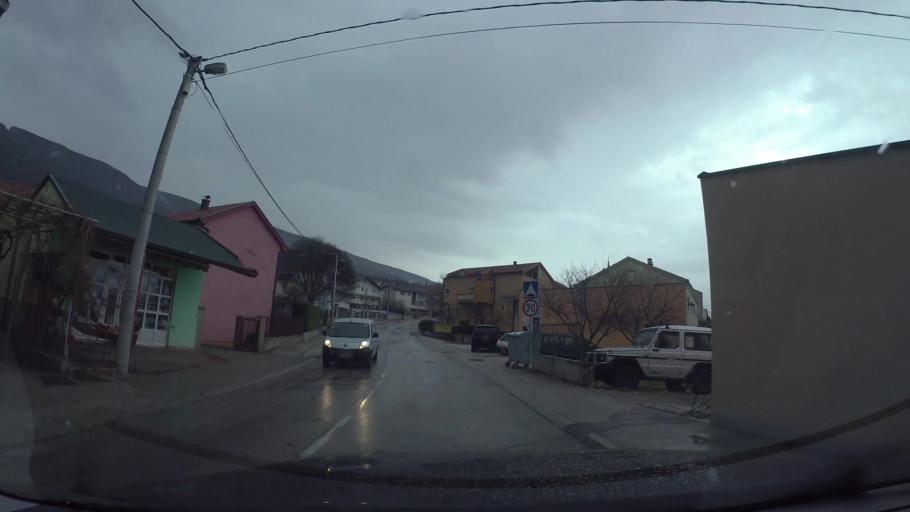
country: BA
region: Federation of Bosnia and Herzegovina
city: Rodoc
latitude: 43.3186
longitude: 17.8342
